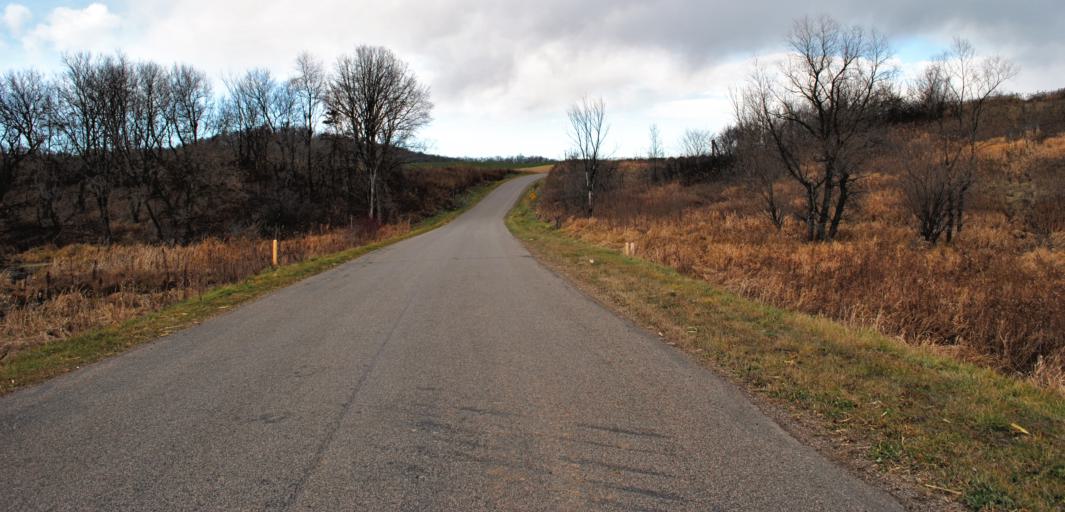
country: US
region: Wisconsin
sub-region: Pepin County
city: Durand
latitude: 44.5032
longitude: -91.9356
